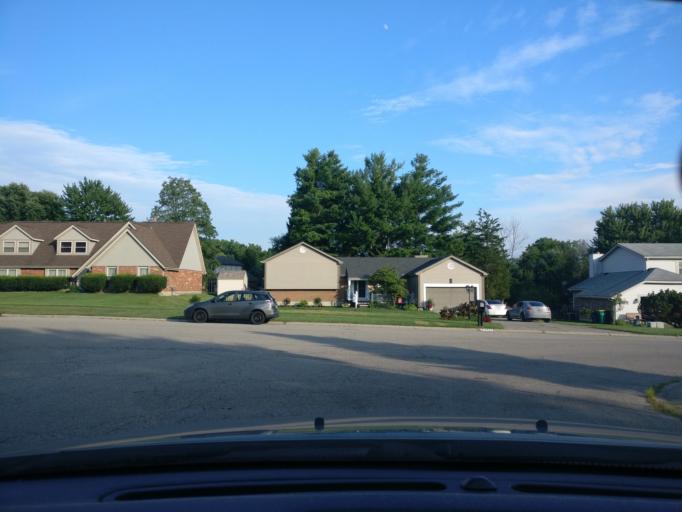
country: US
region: Ohio
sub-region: Warren County
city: Springboro
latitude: 39.5767
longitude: -84.2430
